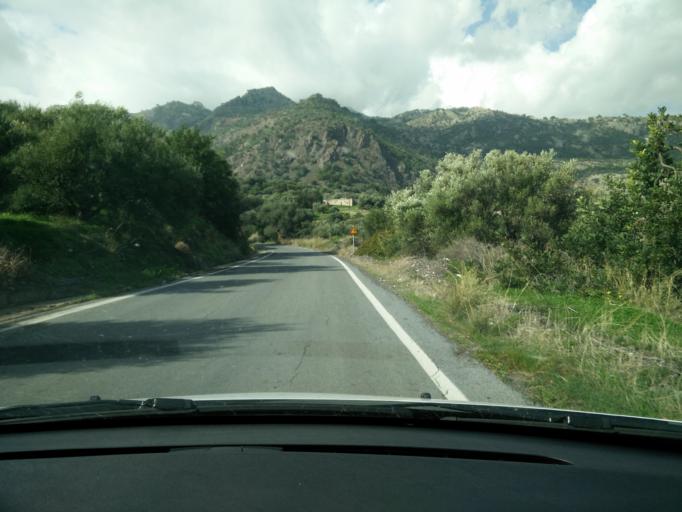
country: GR
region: Crete
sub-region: Nomos Lasithiou
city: Gra Liyia
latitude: 35.0330
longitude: 25.5775
